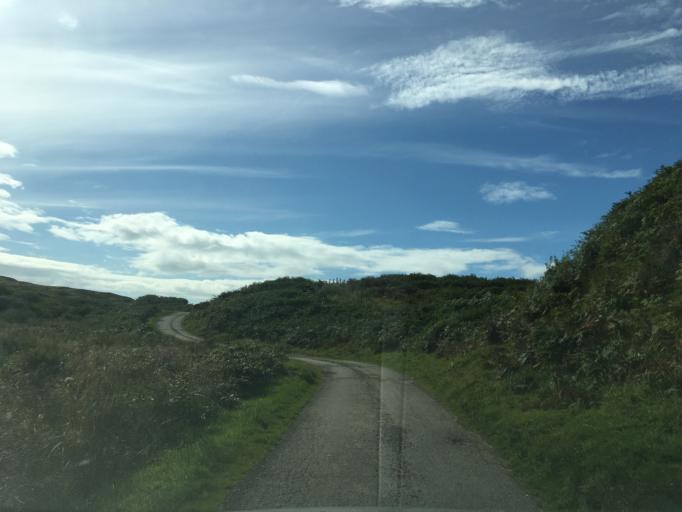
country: GB
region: Scotland
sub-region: Argyll and Bute
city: Oban
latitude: 56.2467
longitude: -5.6296
